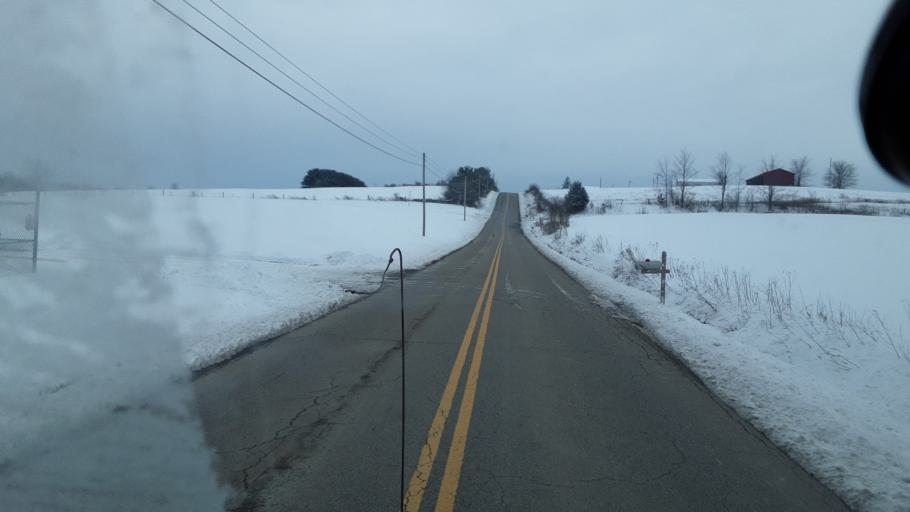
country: US
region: Ohio
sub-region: Perry County
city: Somerset
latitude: 39.9341
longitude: -82.2244
